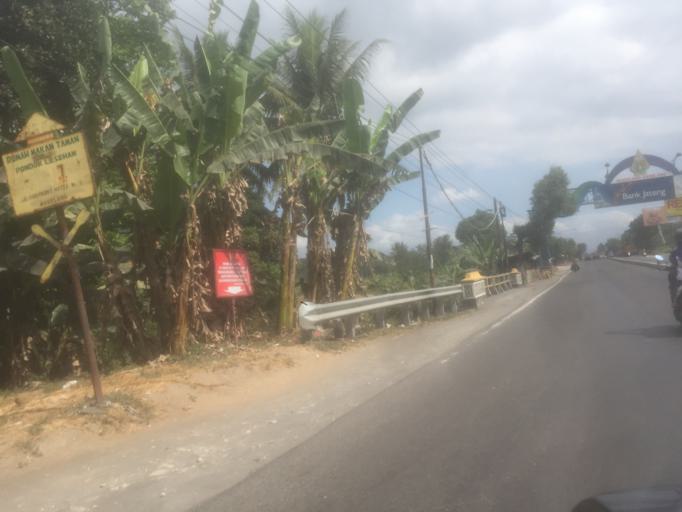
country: ID
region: Central Java
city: Muntilan
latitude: -7.6214
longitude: 110.3119
